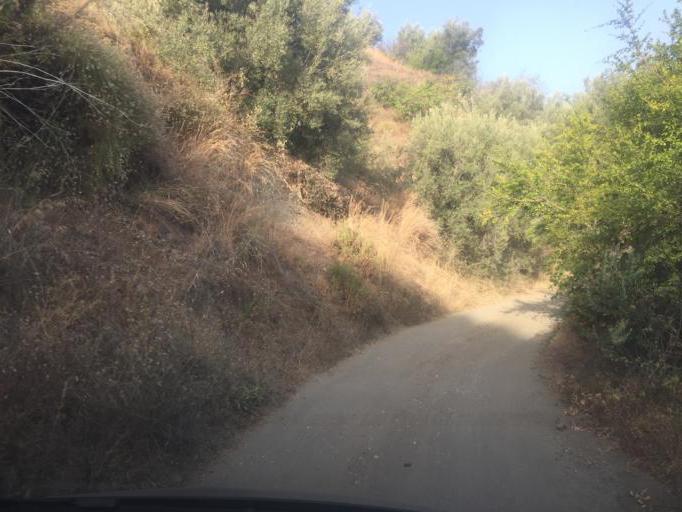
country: ES
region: Andalusia
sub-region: Provincia de Malaga
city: Frigiliana
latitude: 36.8082
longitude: -3.9336
